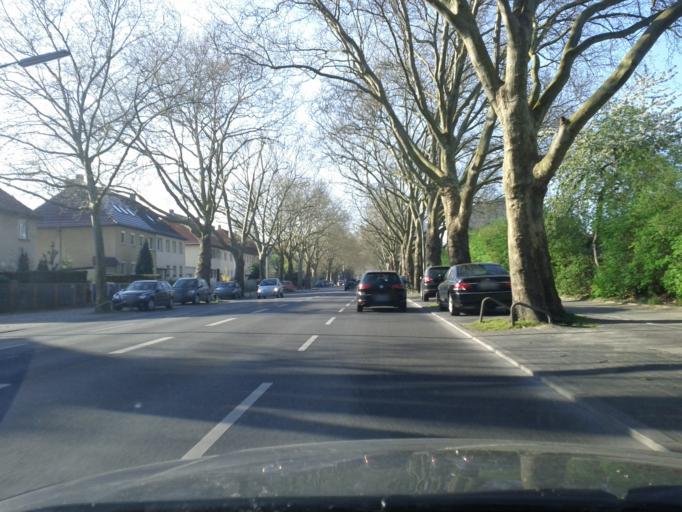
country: DE
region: Berlin
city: Reinickendorf
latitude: 52.5845
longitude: 13.3427
